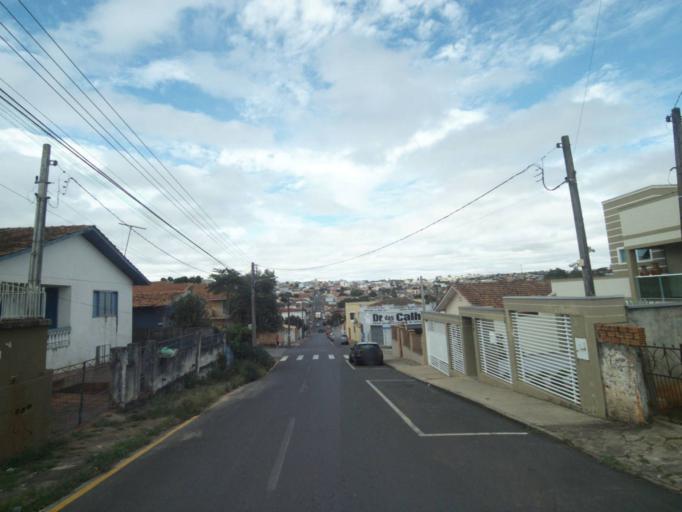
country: BR
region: Parana
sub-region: Telemaco Borba
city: Telemaco Borba
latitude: -24.3231
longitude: -50.6224
